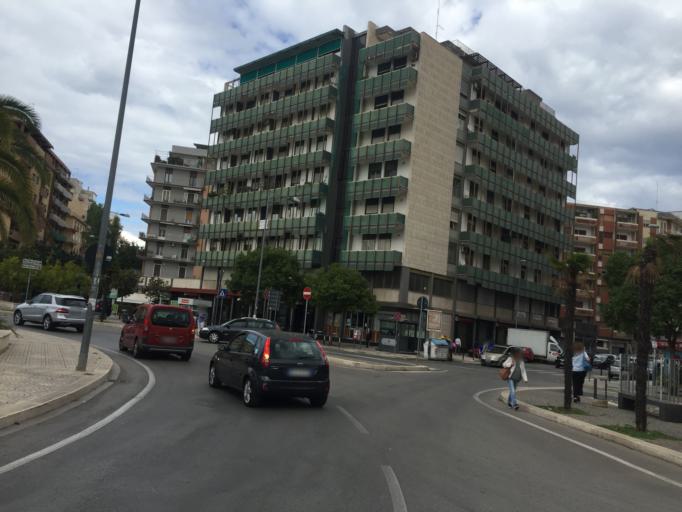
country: IT
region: Apulia
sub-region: Provincia di Bari
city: Bari
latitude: 41.1121
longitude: 16.8632
